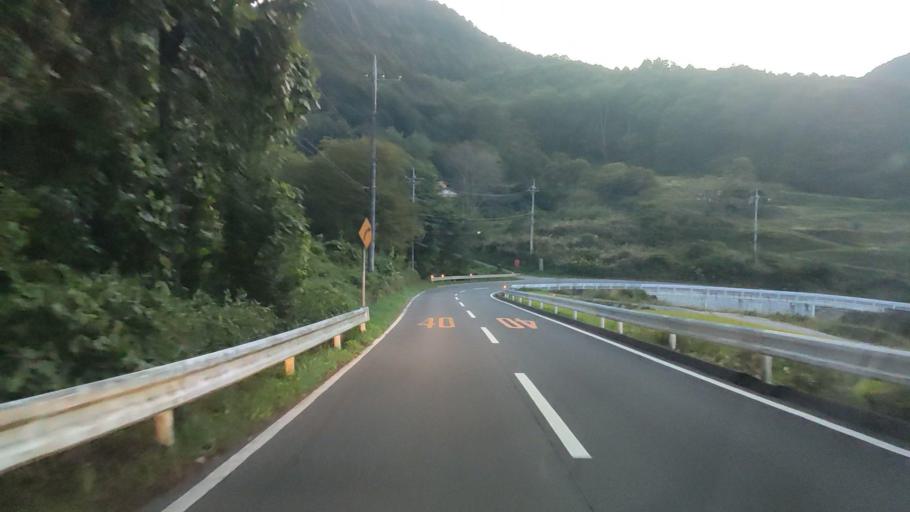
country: JP
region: Gunma
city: Nakanojomachi
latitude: 36.5410
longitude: 138.6041
